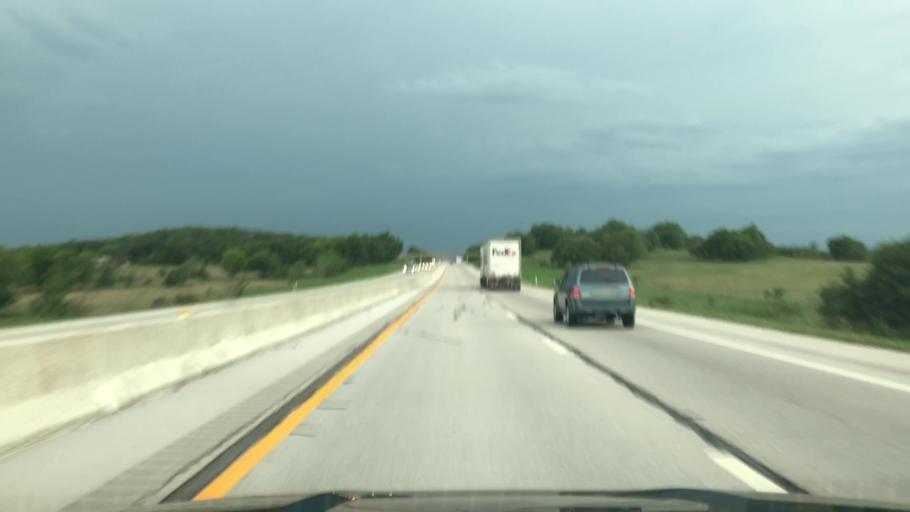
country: US
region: Oklahoma
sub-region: Rogers County
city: Justice
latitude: 36.3437
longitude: -95.4842
